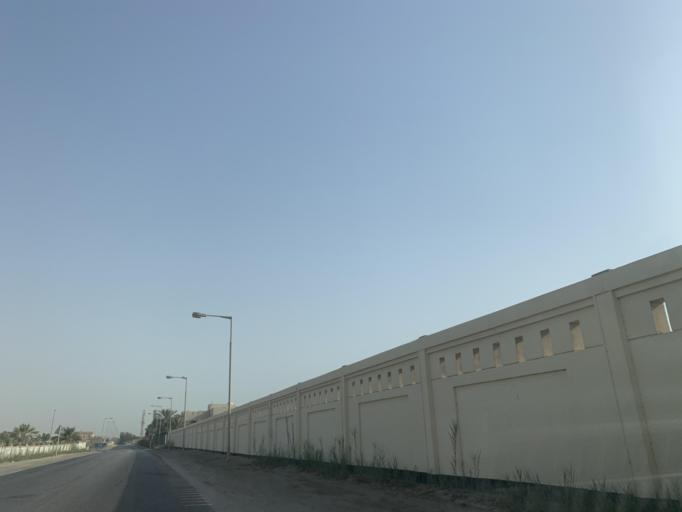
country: BH
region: Central Governorate
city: Madinat Hamad
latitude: 26.1804
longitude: 50.4678
